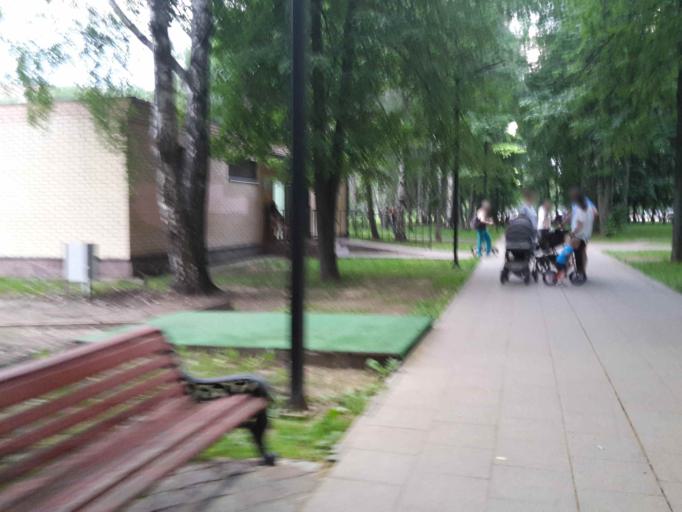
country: RU
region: Moskovskaya
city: Dolgoprudnyy
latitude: 55.9437
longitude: 37.5007
